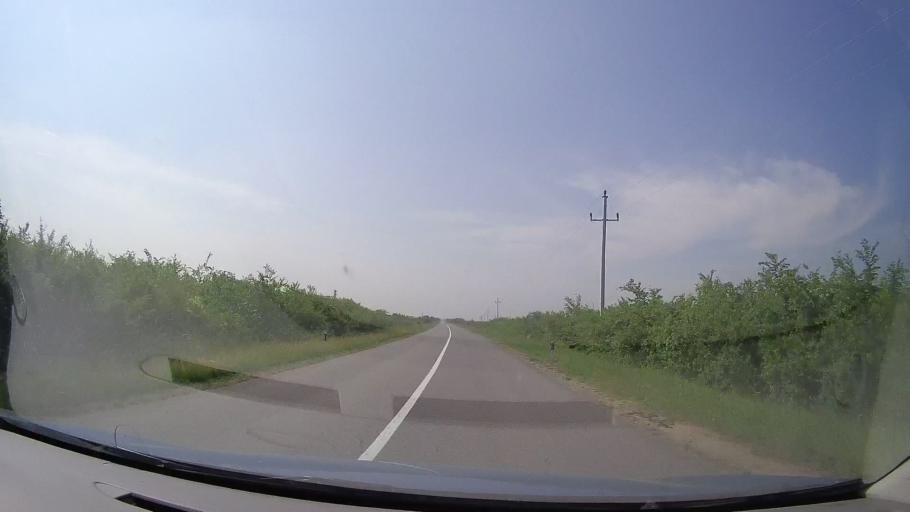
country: RS
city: Jarkovac
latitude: 45.2584
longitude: 20.7637
